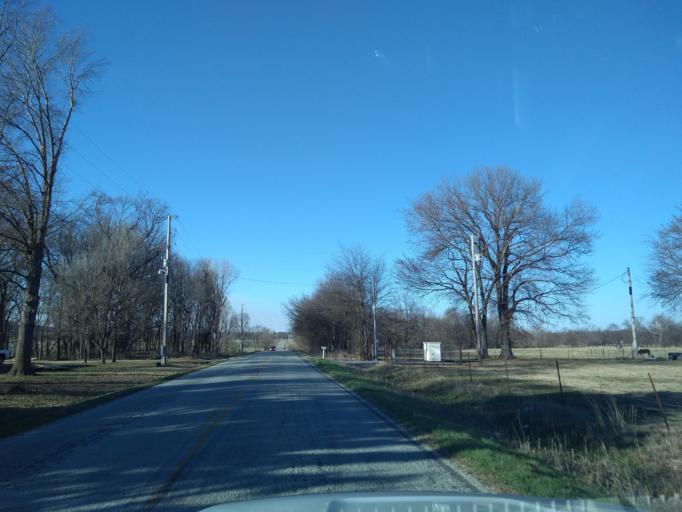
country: US
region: Arkansas
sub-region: Washington County
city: Lincoln
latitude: 36.0050
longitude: -94.3927
